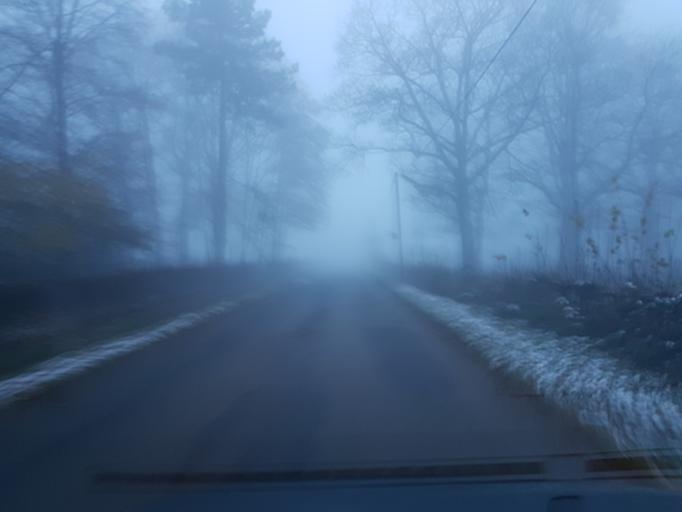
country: BE
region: Wallonia
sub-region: Province de Liege
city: Theux
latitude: 50.4970
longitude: 5.7784
